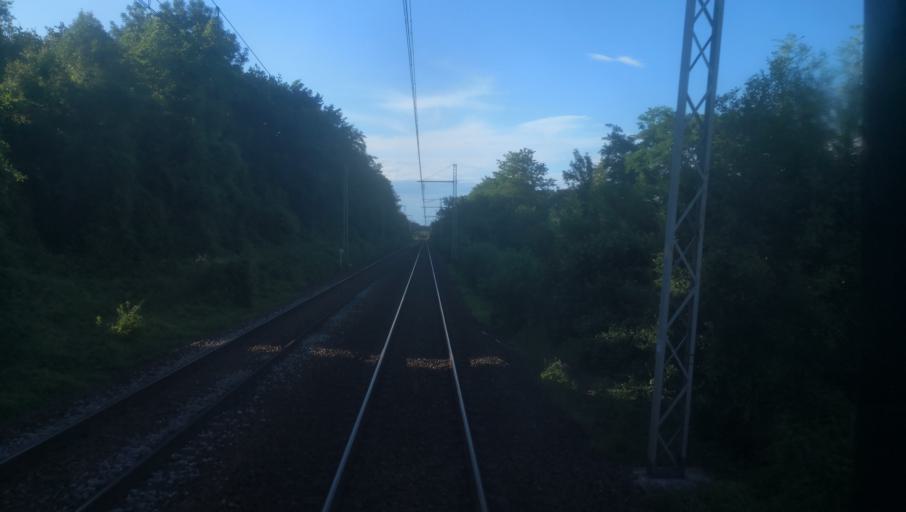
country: FR
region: Centre
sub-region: Departement de l'Indre
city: Reuilly
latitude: 47.0790
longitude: 2.0481
